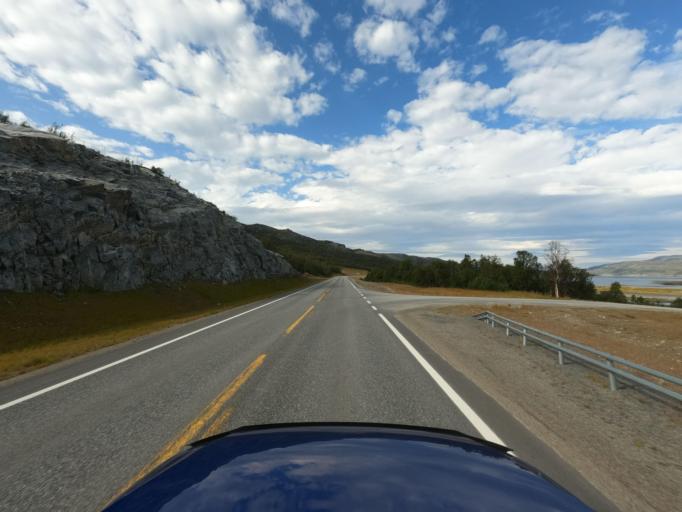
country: NO
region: Finnmark Fylke
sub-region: Kvalsund
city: Kvalsund
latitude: 70.4467
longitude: 24.3098
